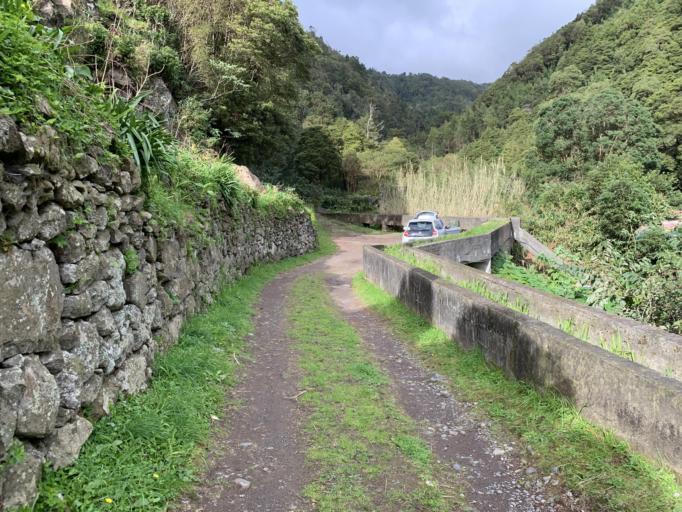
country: PT
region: Azores
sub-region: Povoacao
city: Furnas
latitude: 37.7505
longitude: -25.2023
